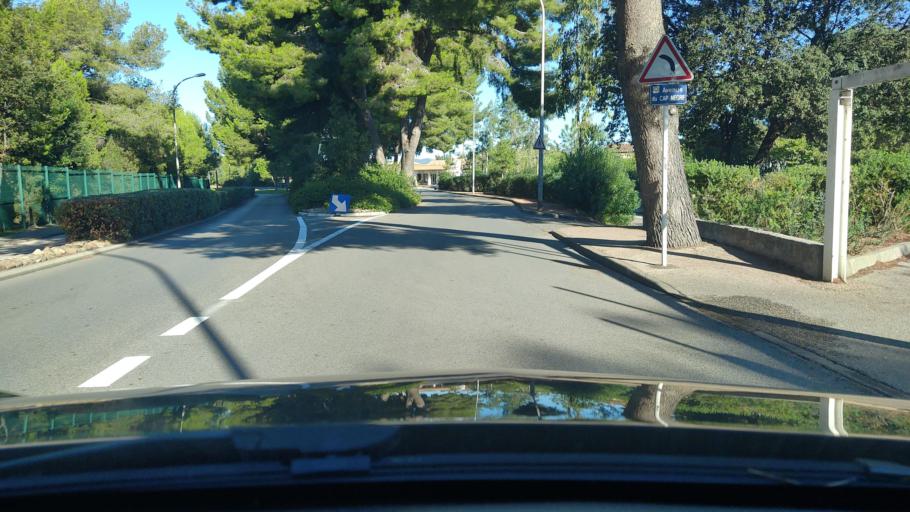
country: FR
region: Provence-Alpes-Cote d'Azur
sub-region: Departement du Var
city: Sanary-sur-Mer
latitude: 43.0991
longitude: 5.8202
